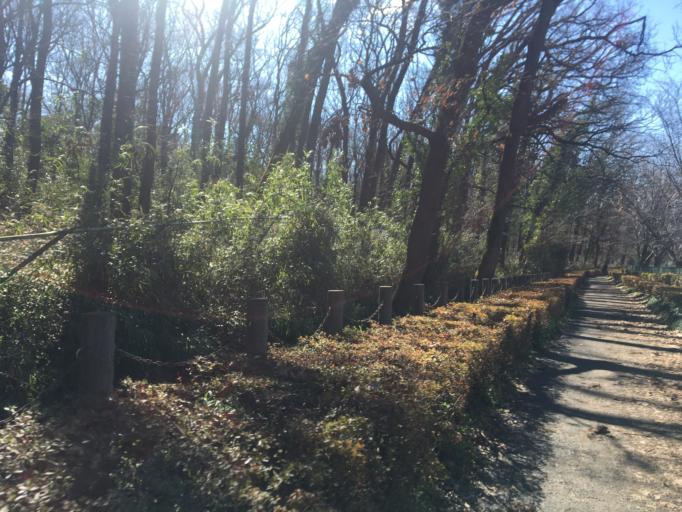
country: JP
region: Saitama
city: Asaka
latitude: 35.7924
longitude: 139.5566
